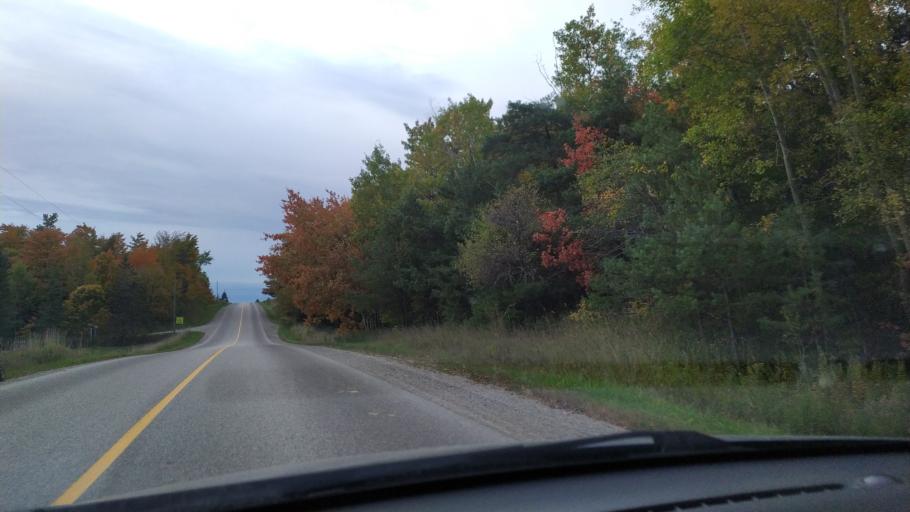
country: CA
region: Ontario
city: Waterloo
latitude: 43.5091
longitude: -80.7054
